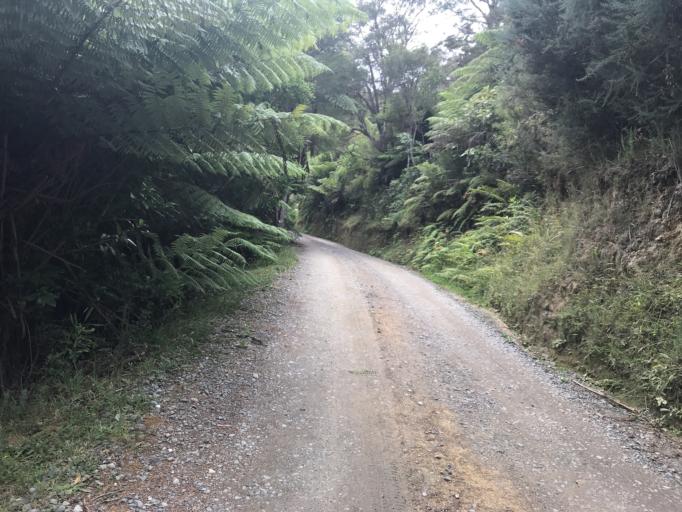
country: NZ
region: Marlborough
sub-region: Marlborough District
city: Picton
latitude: -41.2222
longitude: 173.9726
